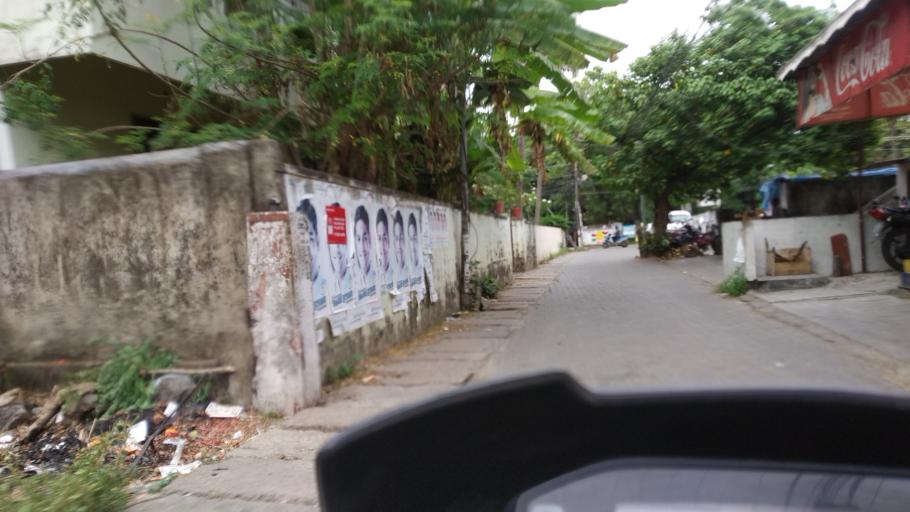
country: IN
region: Kerala
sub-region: Ernakulam
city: Cochin
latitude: 9.9554
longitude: 76.3019
